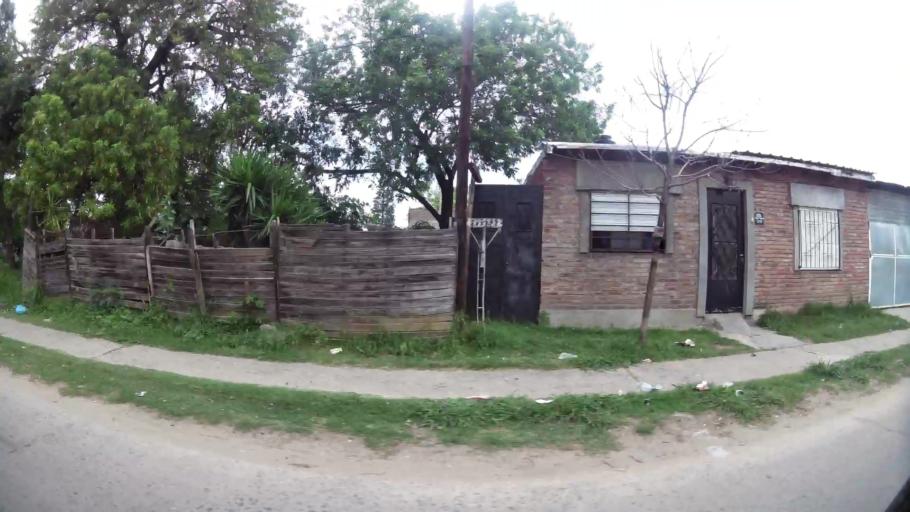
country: AR
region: Santa Fe
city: Gobernador Galvez
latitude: -32.9985
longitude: -60.6572
